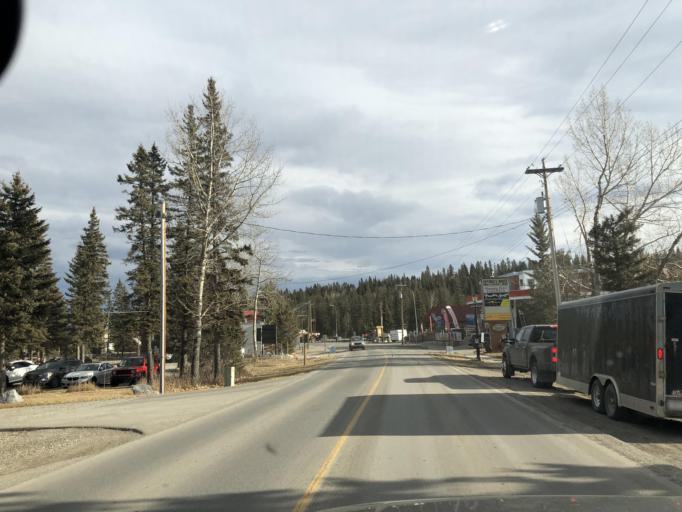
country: CA
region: Alberta
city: Cochrane
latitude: 50.9526
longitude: -114.5622
